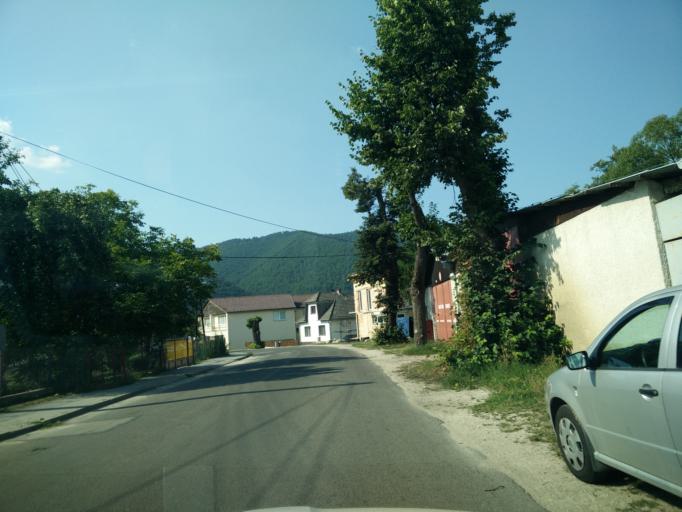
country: SK
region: Zilinsky
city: Rajec
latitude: 49.1227
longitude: 18.6875
